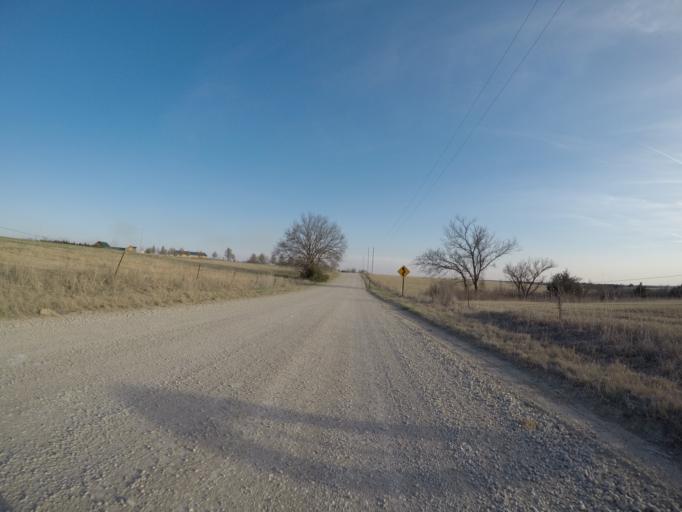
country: US
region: Kansas
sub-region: Riley County
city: Ogden
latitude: 39.2409
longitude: -96.6958
